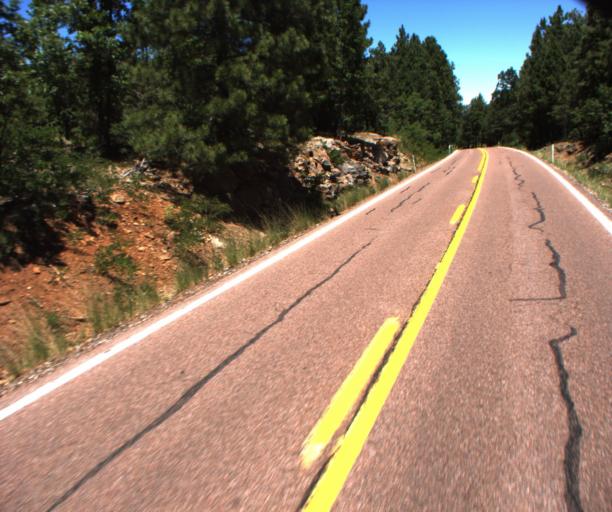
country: US
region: Arizona
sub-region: Gila County
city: Pine
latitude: 34.4713
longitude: -111.3814
